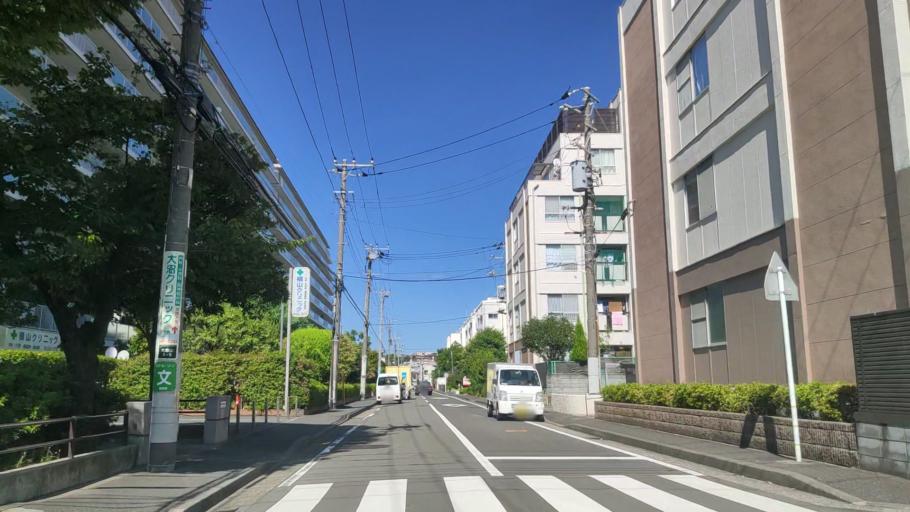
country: JP
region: Kanagawa
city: Yokohama
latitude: 35.5181
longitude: 139.6241
